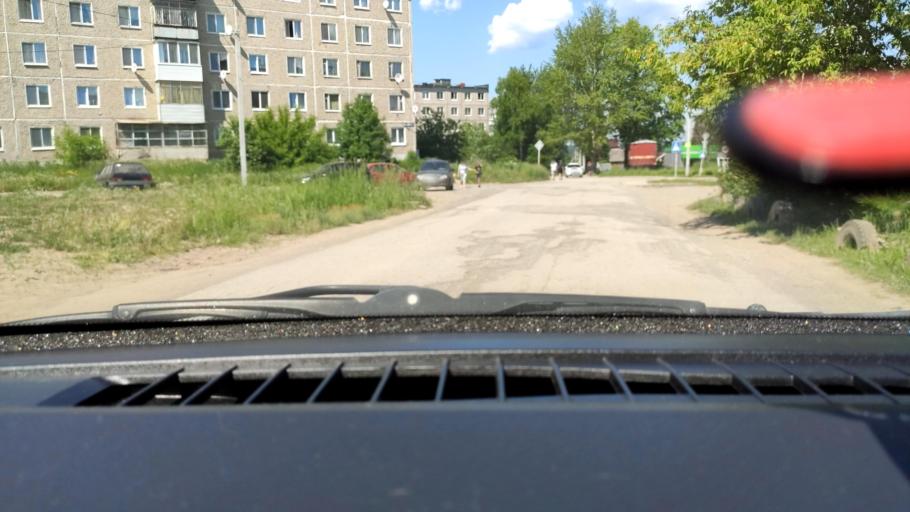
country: RU
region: Perm
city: Sylva
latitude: 58.0321
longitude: 56.7508
